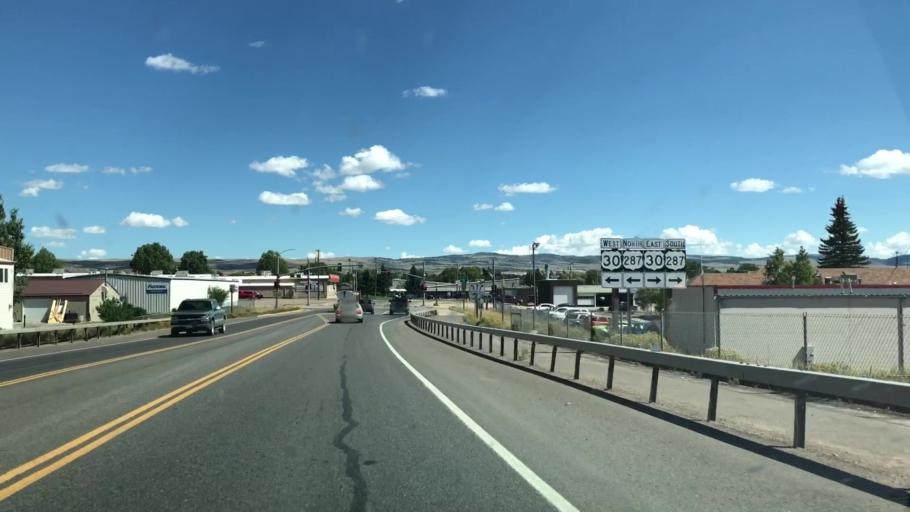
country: US
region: Wyoming
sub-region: Albany County
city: Laramie
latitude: 41.3271
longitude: -105.5937
